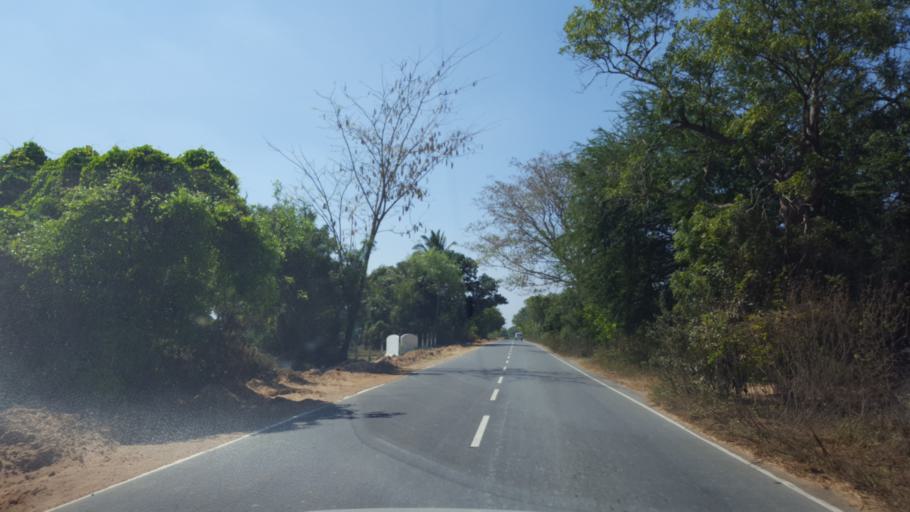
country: IN
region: Tamil Nadu
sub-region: Kancheepuram
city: Wallajahbad
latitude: 12.7717
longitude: 79.8933
